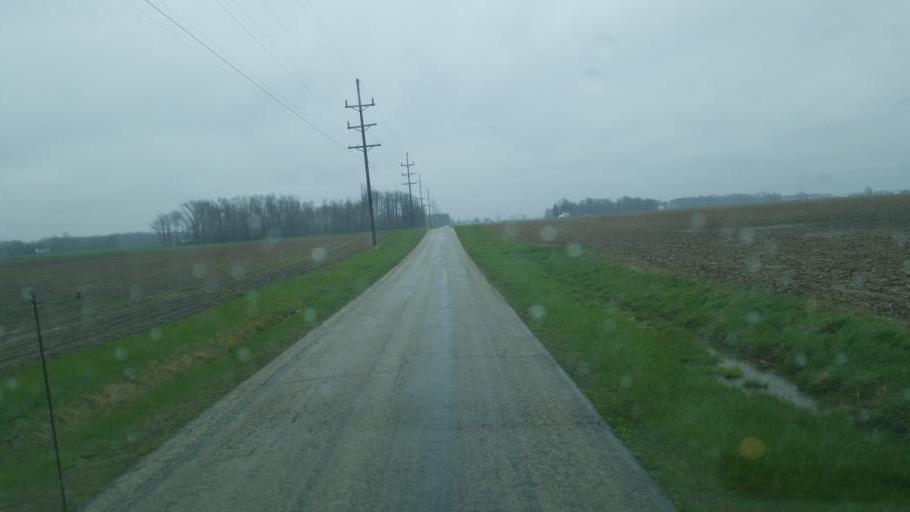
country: US
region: Ohio
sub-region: Crawford County
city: Bucyrus
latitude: 40.8339
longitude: -83.0859
